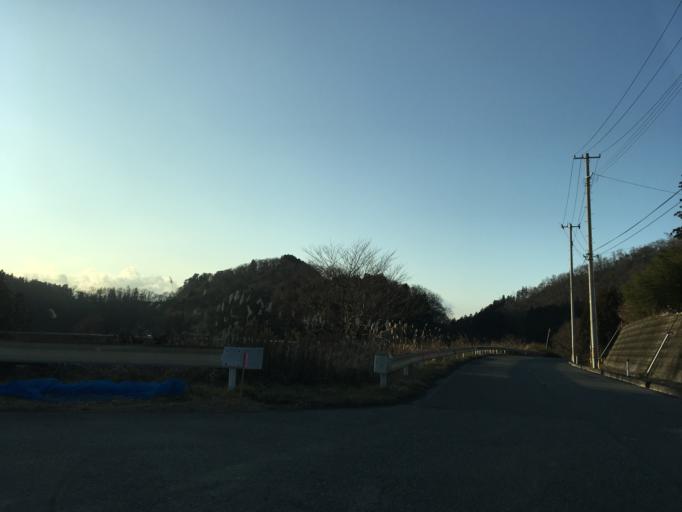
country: JP
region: Iwate
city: Ichinoseki
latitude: 38.8023
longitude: 141.2322
